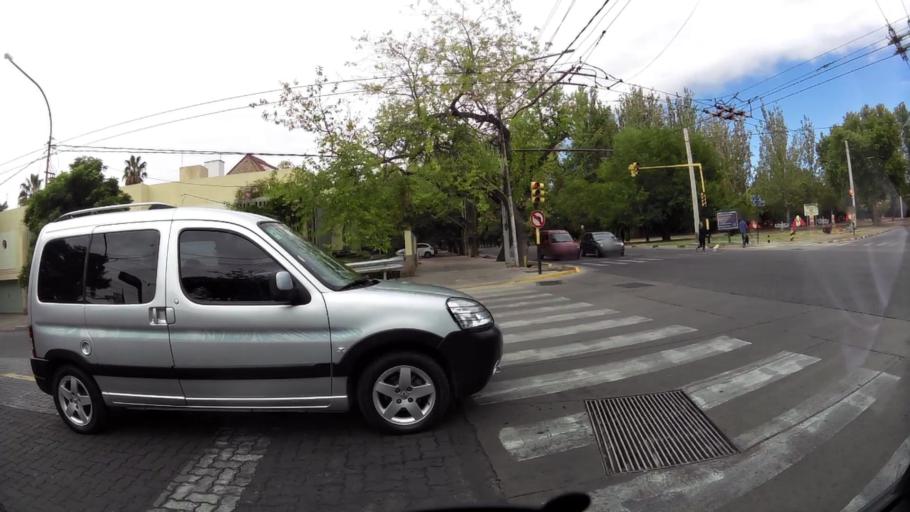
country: AR
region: Mendoza
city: Mendoza
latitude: -32.8835
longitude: -68.8605
